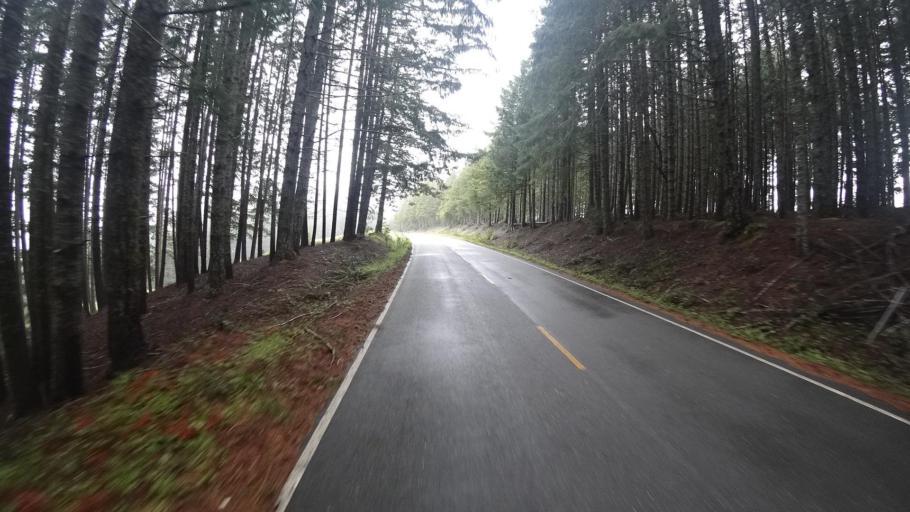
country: US
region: California
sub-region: Humboldt County
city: Westhaven-Moonstone
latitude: 41.2030
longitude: -123.9458
